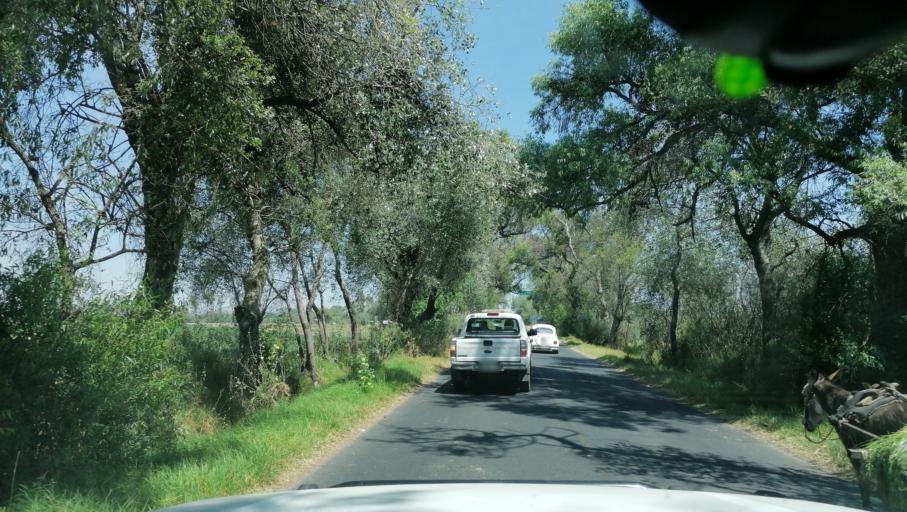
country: MX
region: Tlaxcala
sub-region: Tetlatlahuca
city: Tetlatlahuca
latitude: 19.2075
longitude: -98.2815
